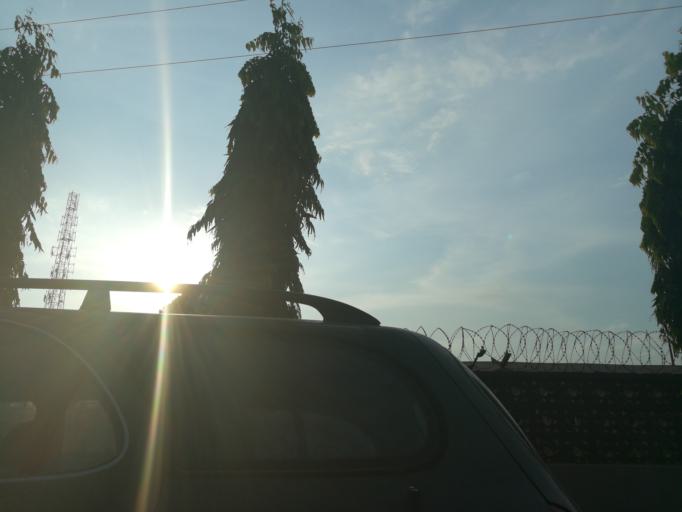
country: NG
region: Lagos
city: Ojota
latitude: 6.5871
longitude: 3.3964
